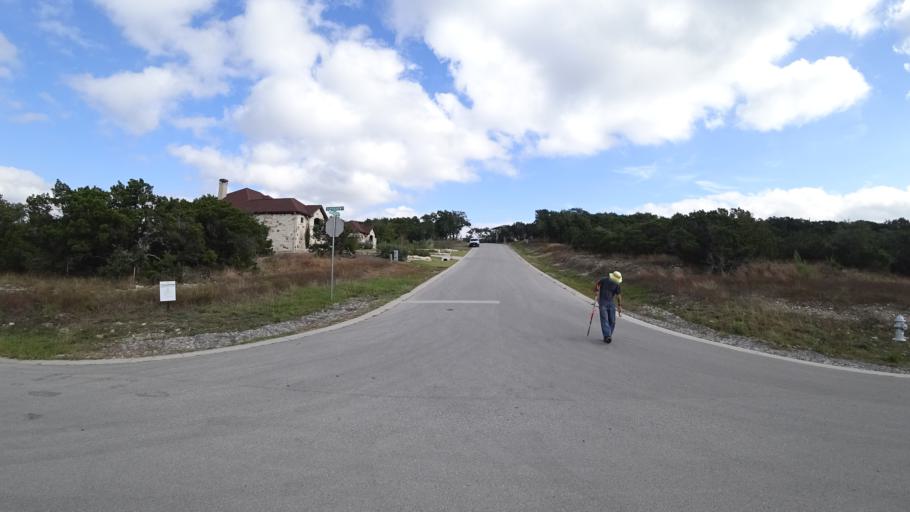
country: US
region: Texas
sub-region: Travis County
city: Bee Cave
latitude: 30.2552
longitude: -97.9285
